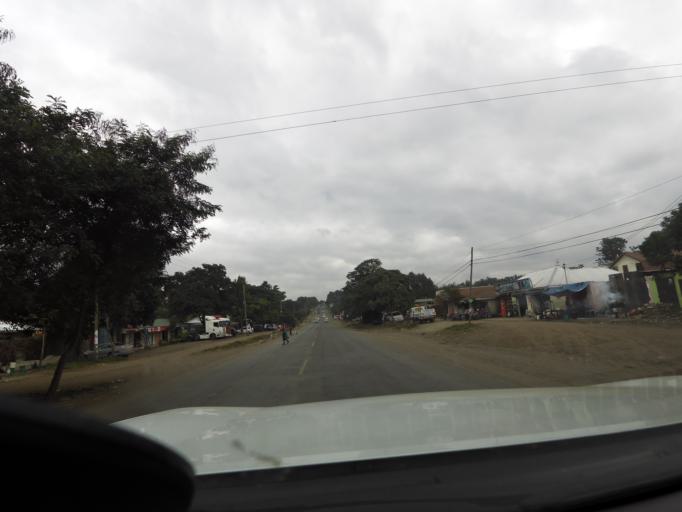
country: TZ
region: Arusha
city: Arusha
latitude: -3.3623
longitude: 36.6676
